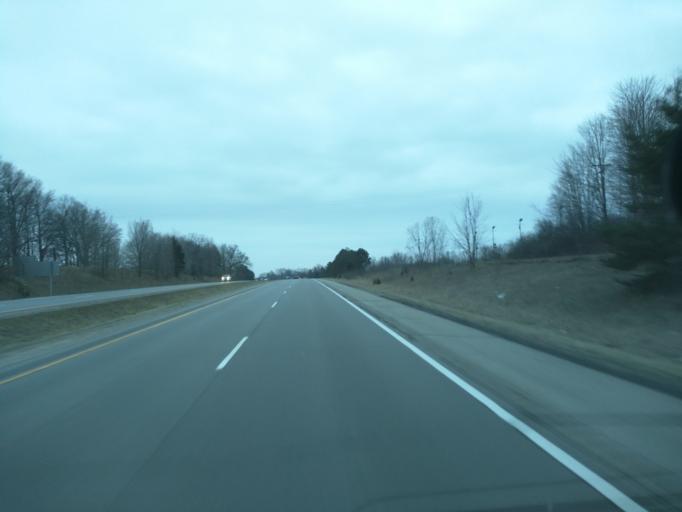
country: US
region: Michigan
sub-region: Ingham County
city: Leslie
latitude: 42.4446
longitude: -84.4437
